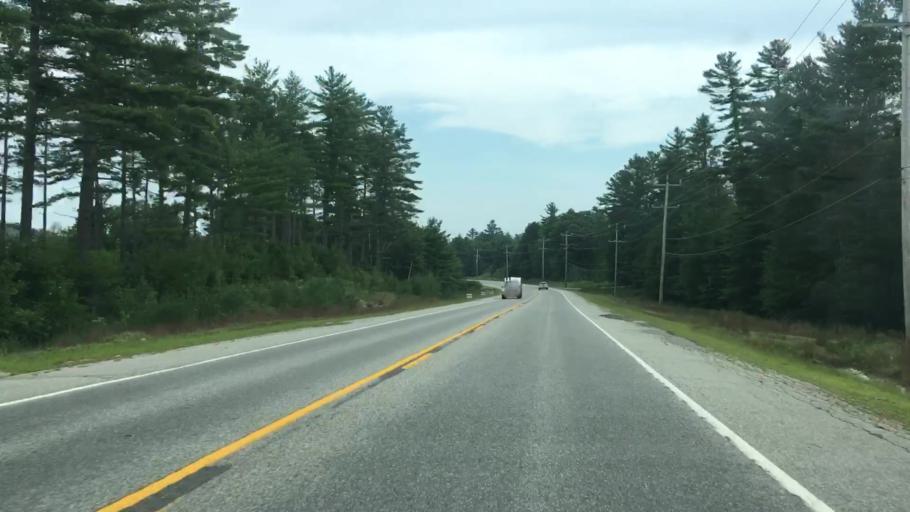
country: US
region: Maine
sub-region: Oxford County
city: Bethel
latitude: 44.4366
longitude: -70.8059
